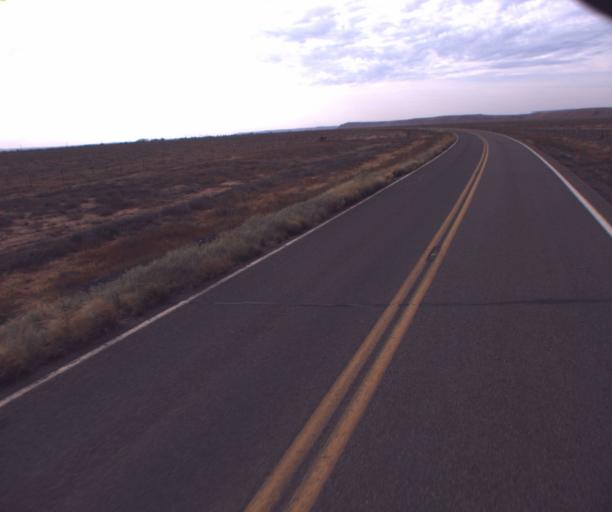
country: US
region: Arizona
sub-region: Apache County
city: Many Farms
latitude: 36.4590
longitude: -109.6065
